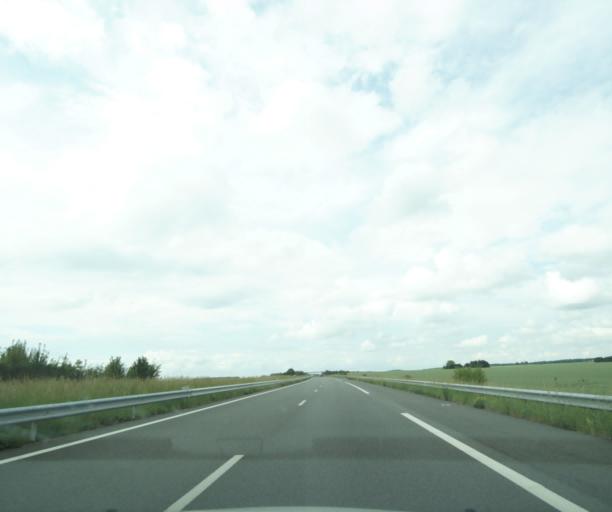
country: FR
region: Centre
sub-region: Departement du Cher
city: Chateauneuf-sur-Cher
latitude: 46.8196
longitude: 2.4129
